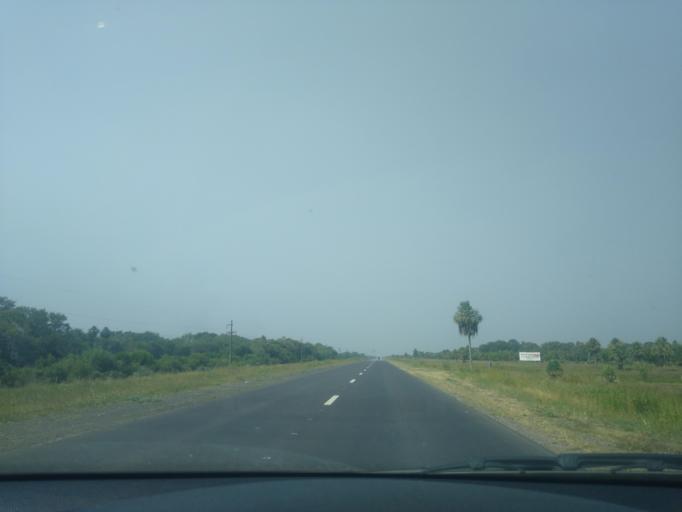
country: AR
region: Chaco
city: Fontana
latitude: -27.5110
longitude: -59.0961
